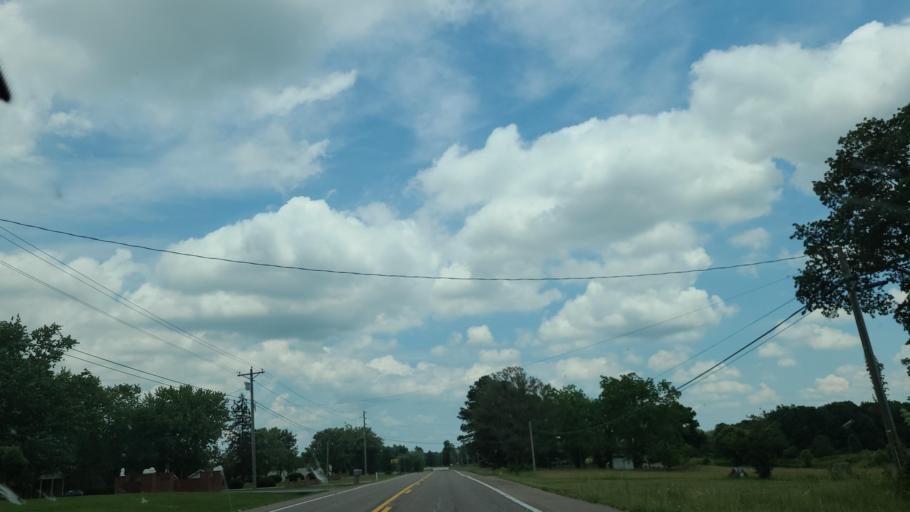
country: US
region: Tennessee
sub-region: Cumberland County
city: Lake Tansi
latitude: 35.8895
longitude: -84.9985
